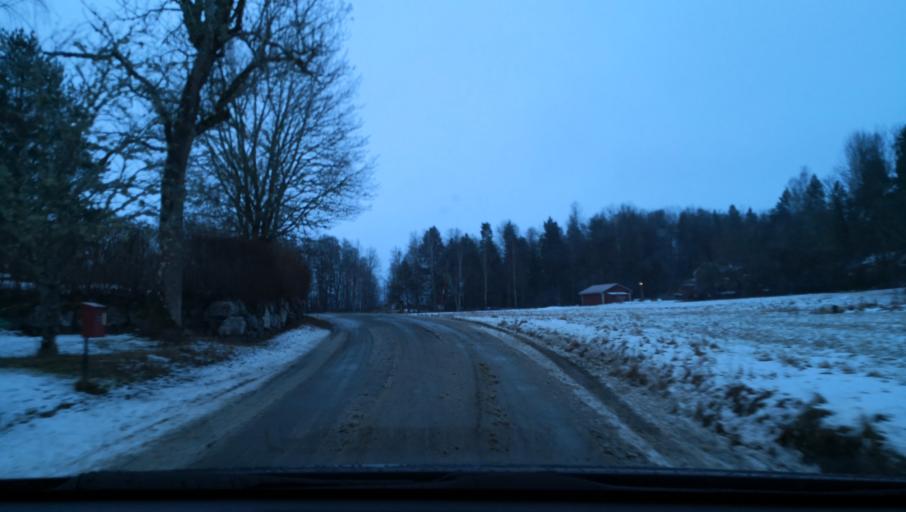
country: SE
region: Vaestmanland
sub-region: Kungsors Kommun
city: Kungsoer
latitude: 59.3973
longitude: 16.2059
